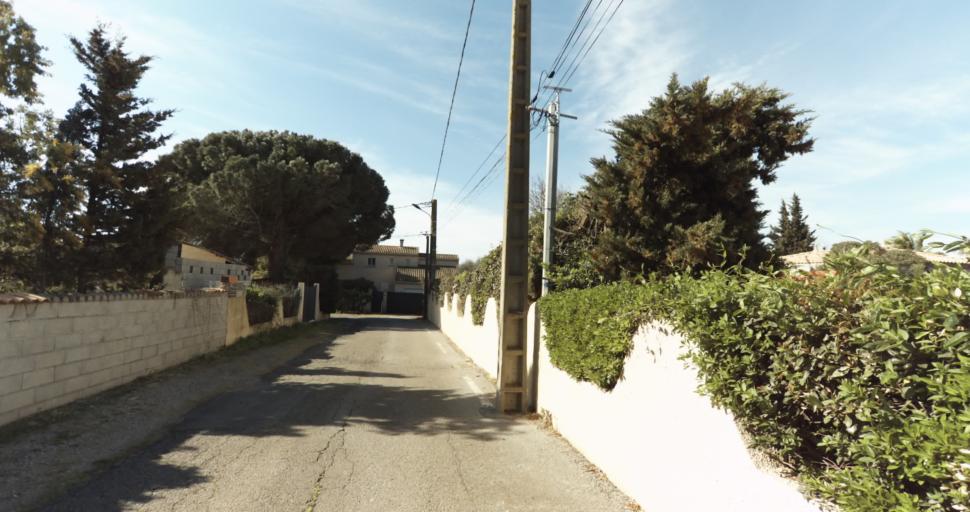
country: FR
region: Languedoc-Roussillon
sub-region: Departement de l'Herault
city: Marseillan
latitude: 43.3368
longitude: 3.5188
